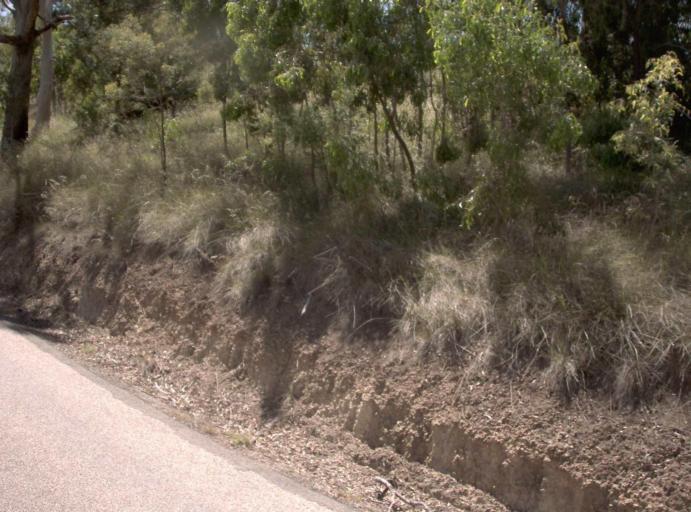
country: AU
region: Victoria
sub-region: East Gippsland
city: Lakes Entrance
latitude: -37.4633
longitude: 148.1945
